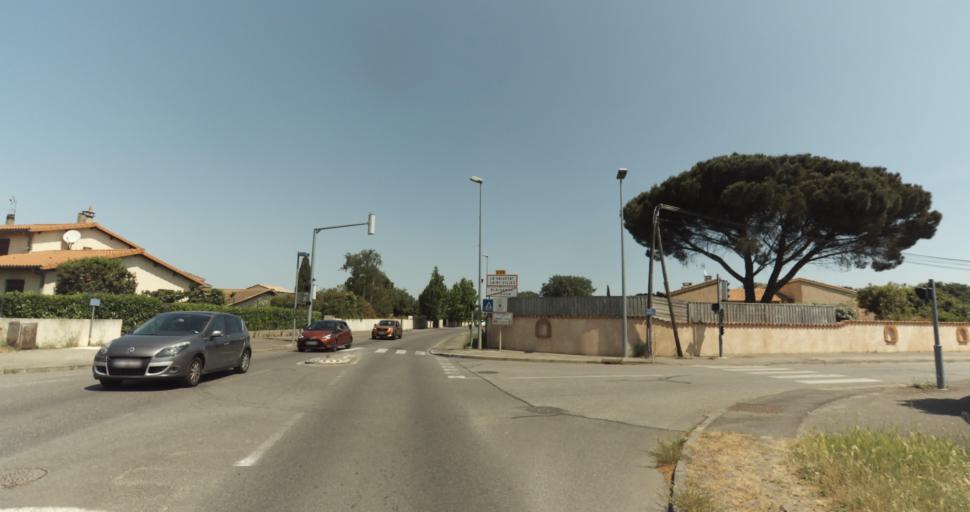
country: FR
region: Midi-Pyrenees
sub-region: Departement de la Haute-Garonne
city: La Salvetat-Saint-Gilles
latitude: 43.5677
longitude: 1.2663
